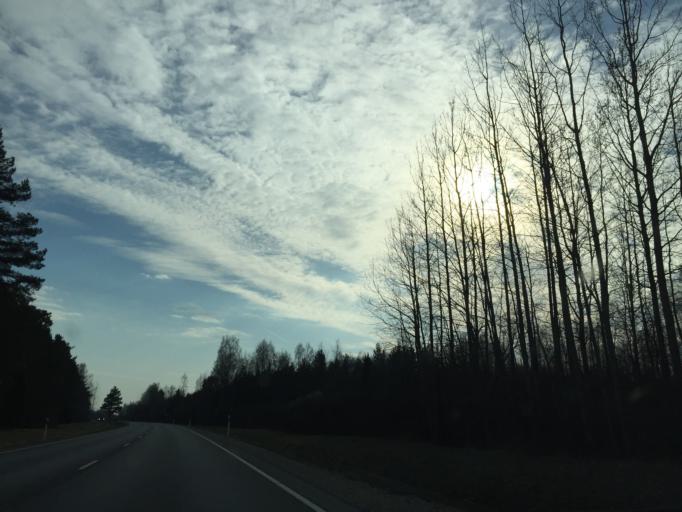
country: EE
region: Jogevamaa
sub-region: Mustvee linn
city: Mustvee
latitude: 58.9327
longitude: 27.0274
